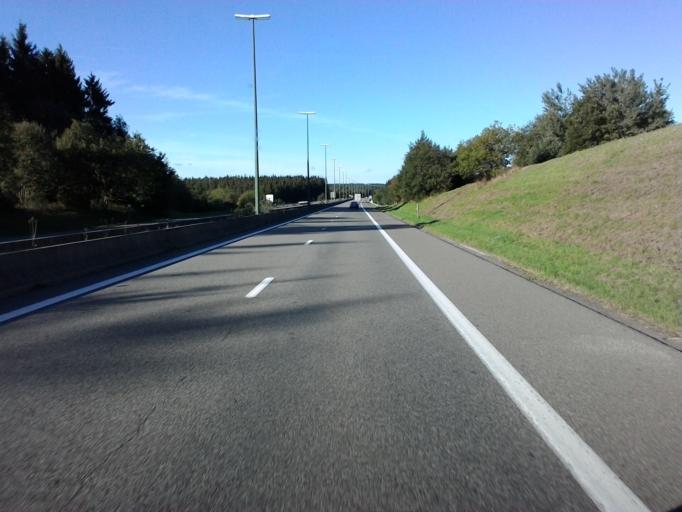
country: BE
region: Wallonia
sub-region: Province du Luxembourg
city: Bastogne
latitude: 50.0273
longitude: 5.6999
